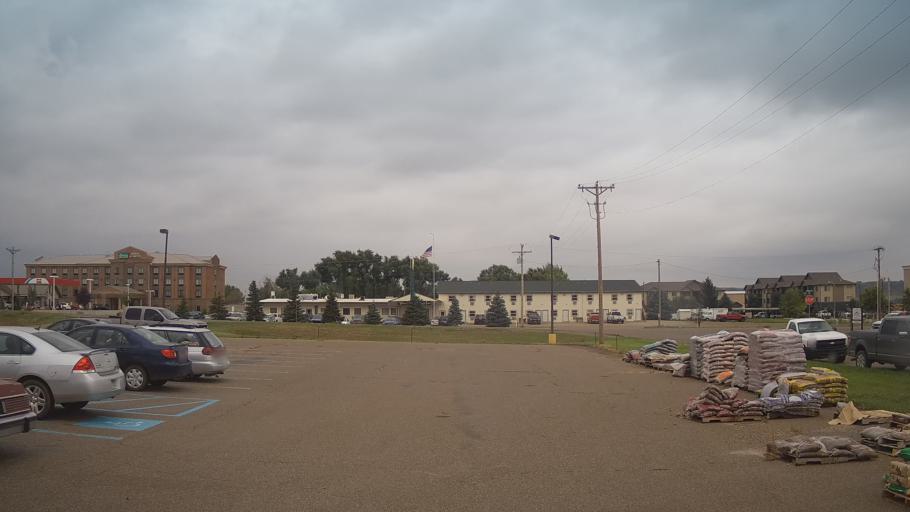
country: US
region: Montana
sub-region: Dawson County
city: Glendive
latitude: 47.1262
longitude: -104.6922
